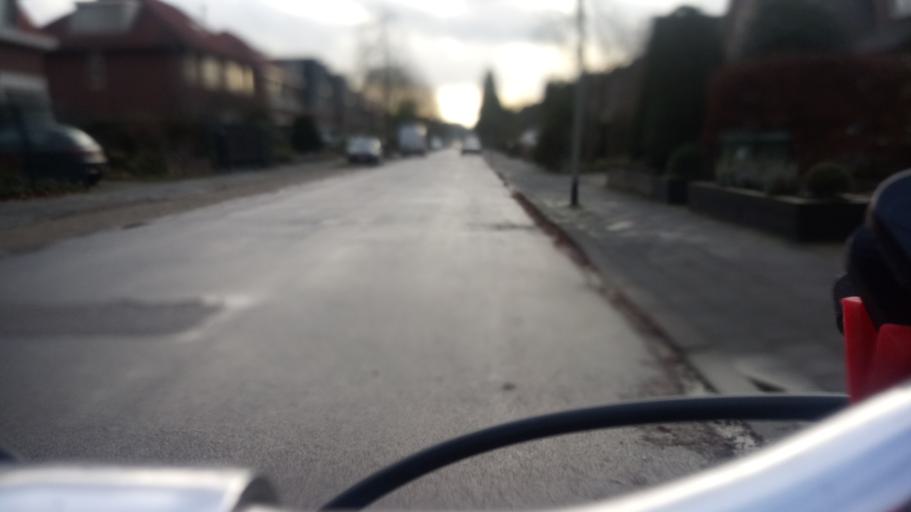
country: NL
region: Gelderland
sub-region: Gemeente Nijmegen
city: Nijmegen
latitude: 51.8218
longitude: 5.8549
